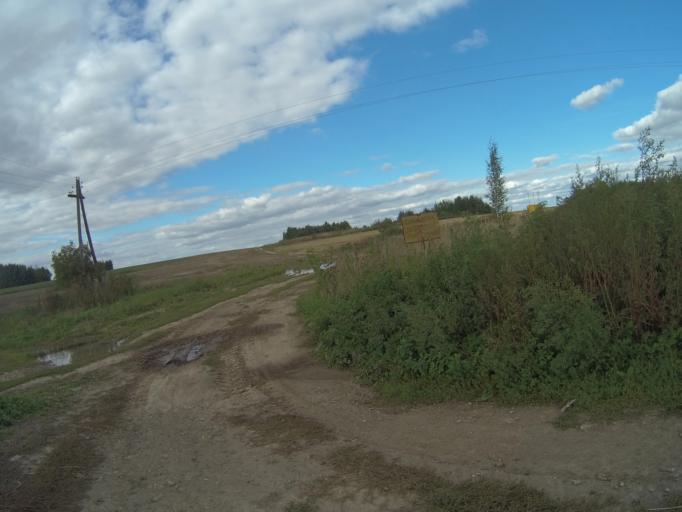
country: RU
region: Vladimir
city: Orgtrud
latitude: 56.3148
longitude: 40.6098
